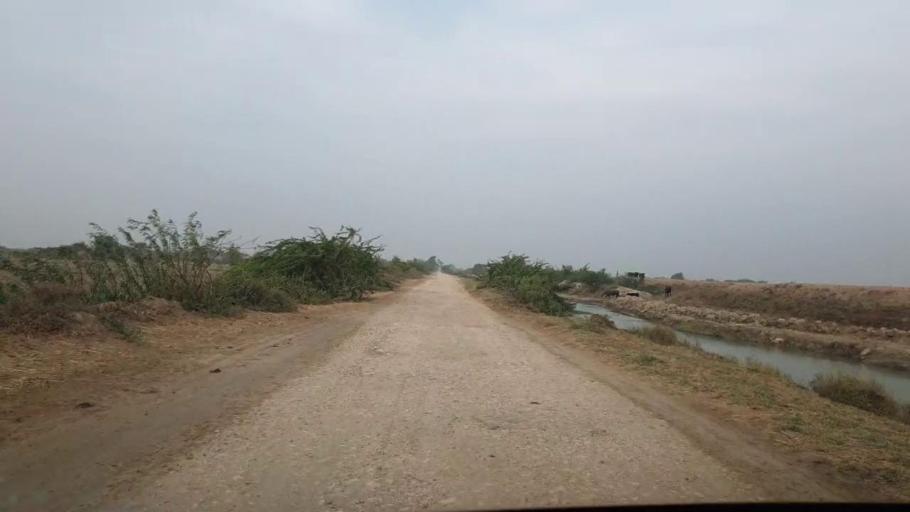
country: PK
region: Sindh
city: Chuhar Jamali
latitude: 24.4100
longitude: 67.9486
